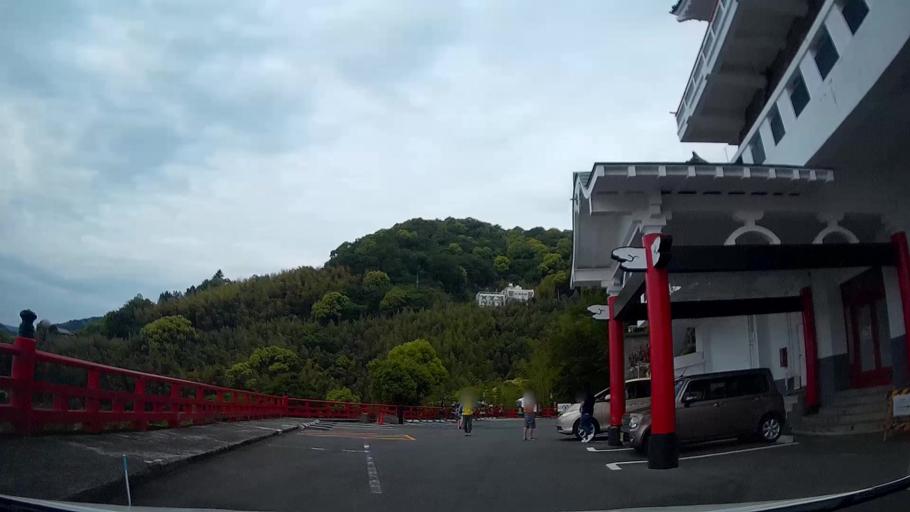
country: JP
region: Shizuoka
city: Atami
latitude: 35.0863
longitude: 139.0787
